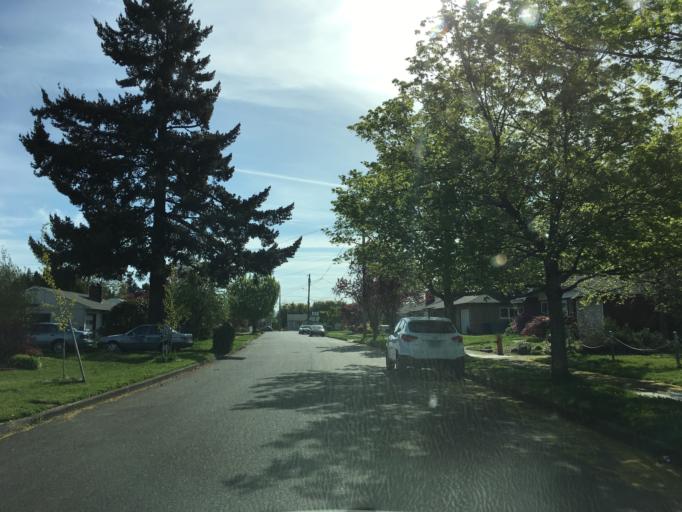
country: US
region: Oregon
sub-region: Multnomah County
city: Lents
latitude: 45.5386
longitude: -122.5408
